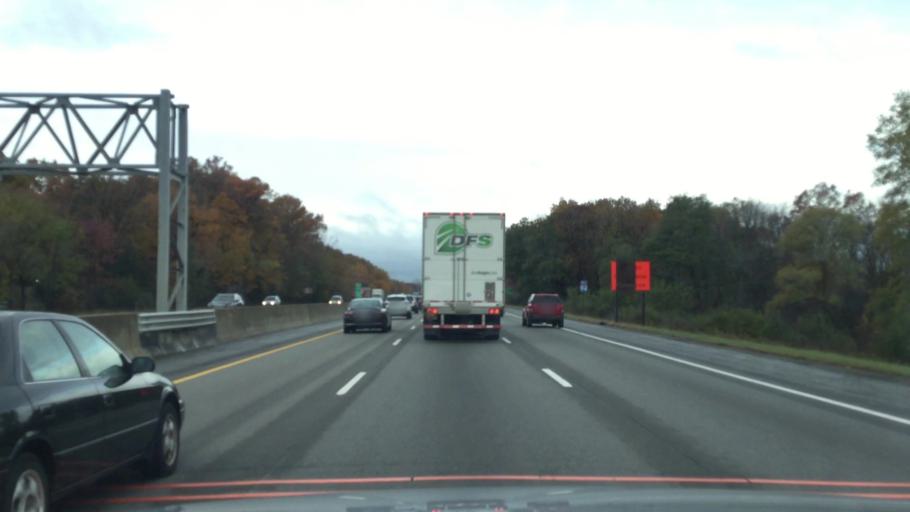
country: US
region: Michigan
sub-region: Washtenaw County
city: Ypsilanti
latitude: 42.2246
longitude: -83.6609
